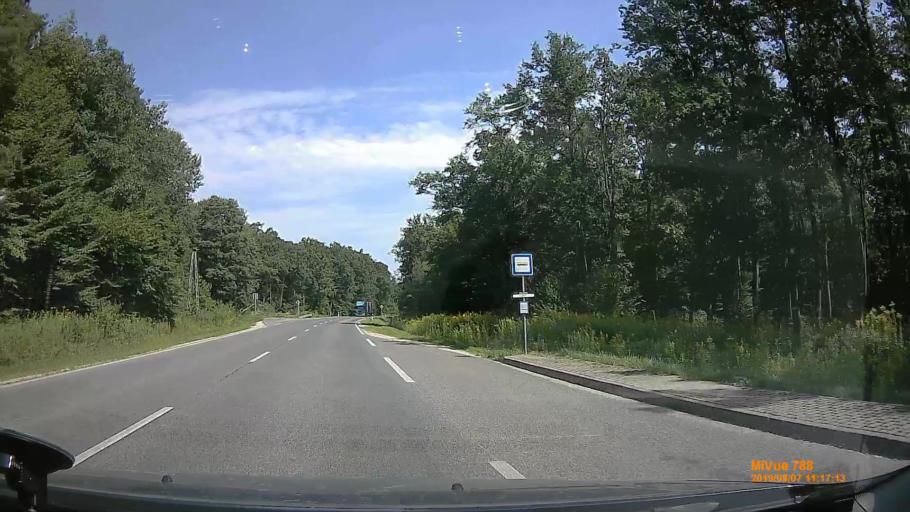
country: HU
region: Zala
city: Zalalovo
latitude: 46.7382
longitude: 16.5535
